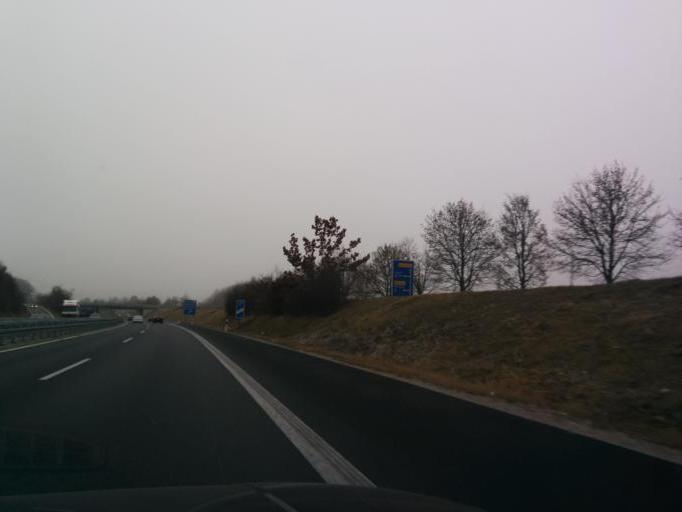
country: DE
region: Bavaria
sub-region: Upper Bavaria
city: Windach
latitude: 48.0744
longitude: 11.0430
